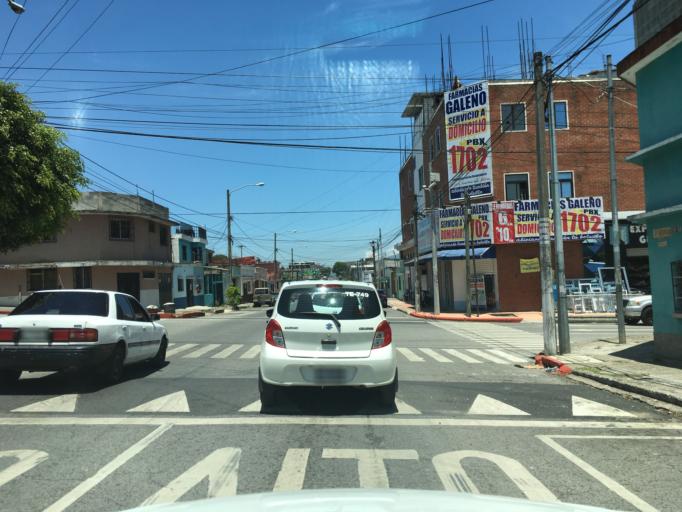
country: GT
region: Guatemala
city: Guatemala City
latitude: 14.6065
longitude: -90.5416
